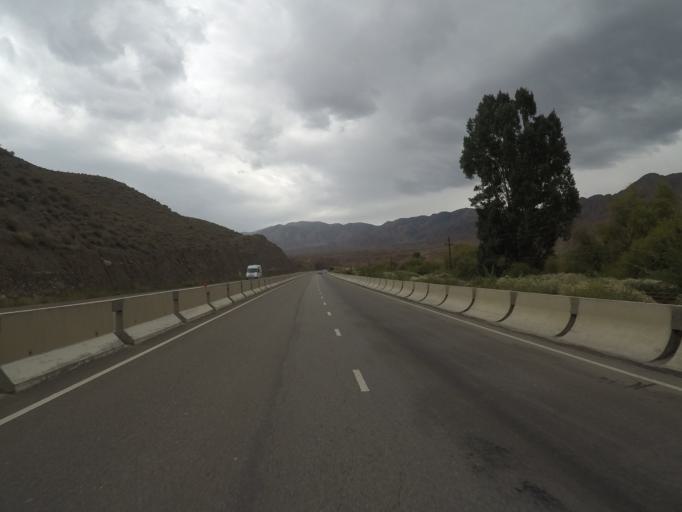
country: KG
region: Naryn
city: Kochkor
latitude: 42.4765
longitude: 75.8721
